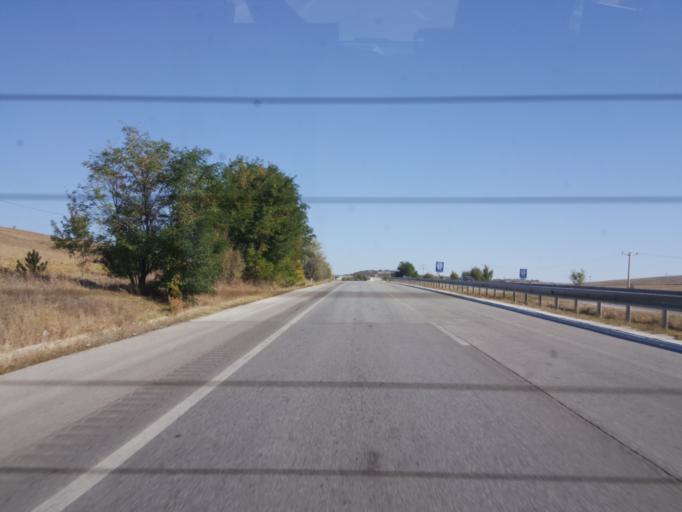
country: TR
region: Corum
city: Alaca
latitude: 40.2881
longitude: 34.6499
